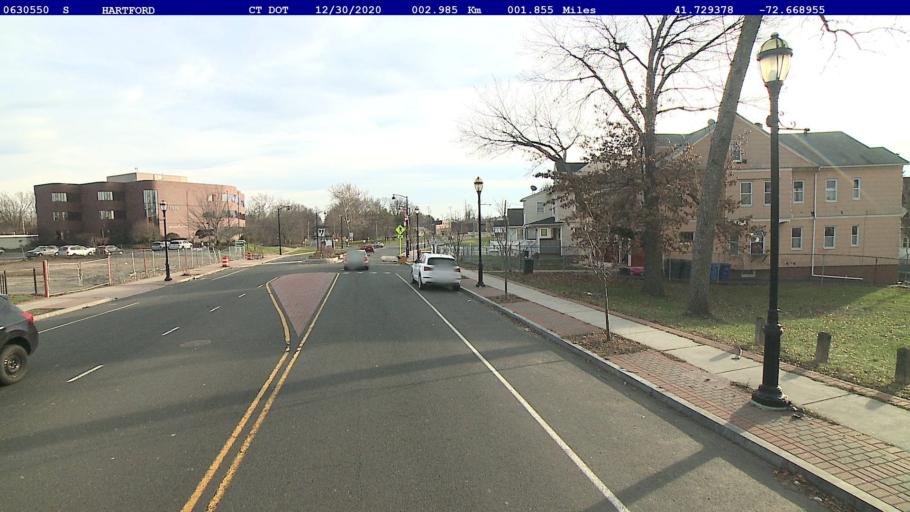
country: US
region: Connecticut
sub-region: Hartford County
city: Wethersfield
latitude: 41.7294
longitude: -72.6690
